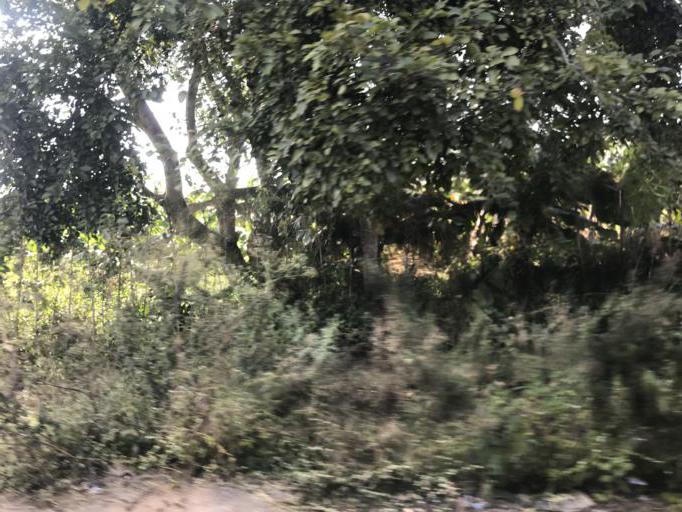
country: IN
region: Karnataka
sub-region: Bangalore Urban
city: Anekal
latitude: 12.8012
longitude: 77.5591
